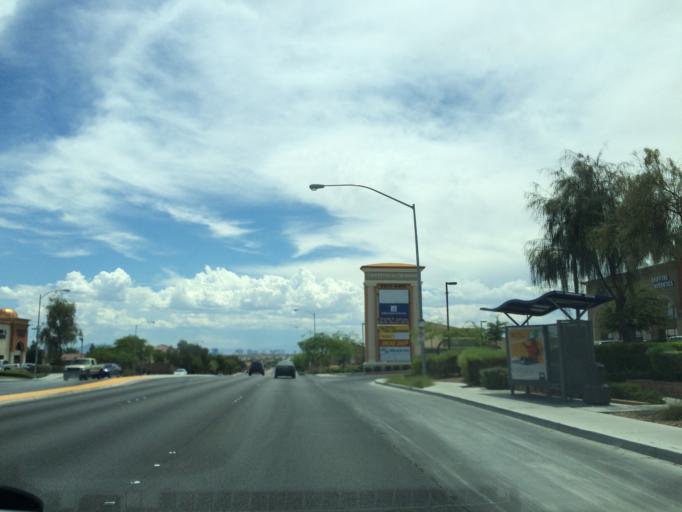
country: US
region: Nevada
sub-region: Clark County
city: North Las Vegas
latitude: 36.2760
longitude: -115.1799
